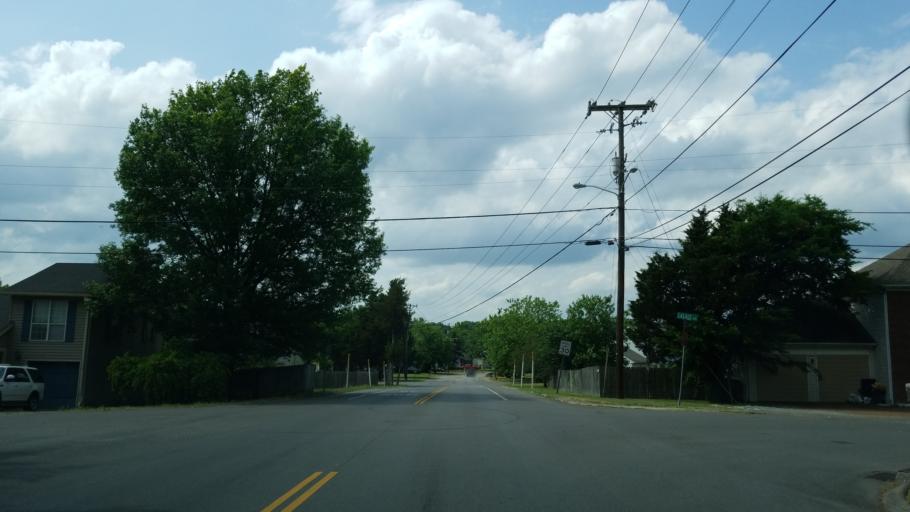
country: US
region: Tennessee
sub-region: Rutherford County
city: La Vergne
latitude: 36.0678
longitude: -86.6230
